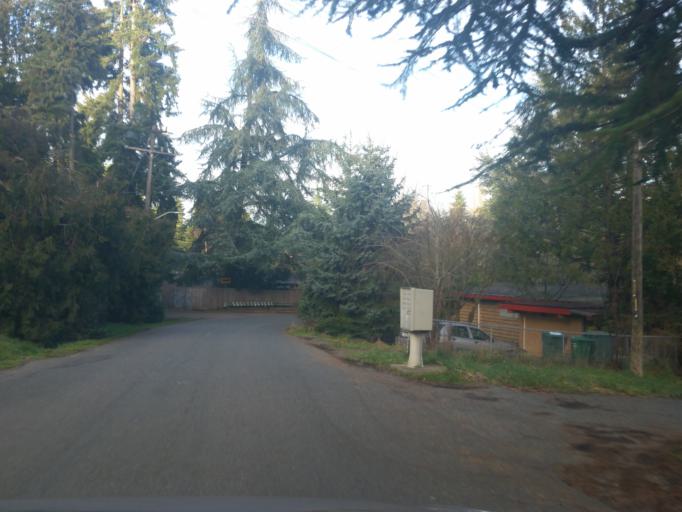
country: US
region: Washington
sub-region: King County
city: Lake Forest Park
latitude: 47.7044
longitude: -122.2999
